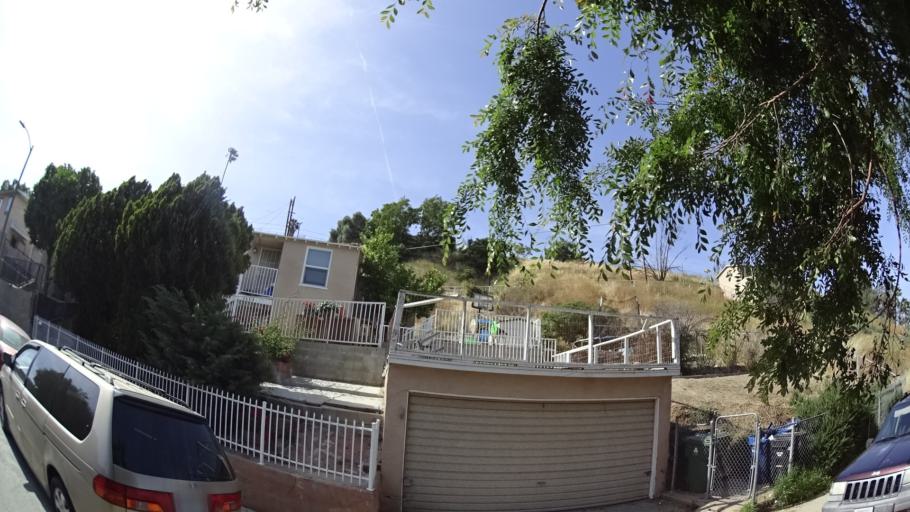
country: US
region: California
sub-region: Los Angeles County
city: Belvedere
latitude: 34.0709
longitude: -118.1770
